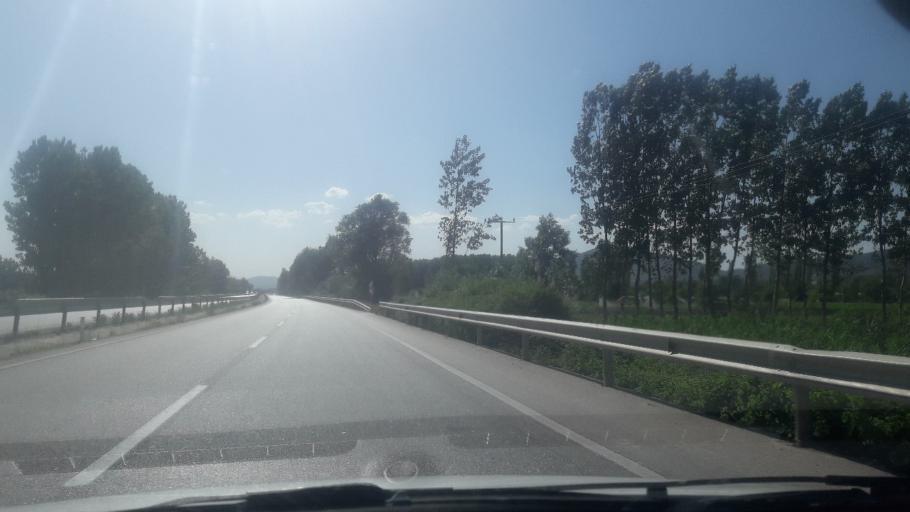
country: TR
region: Tokat
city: Dokmetepe
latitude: 40.3132
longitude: 36.2747
